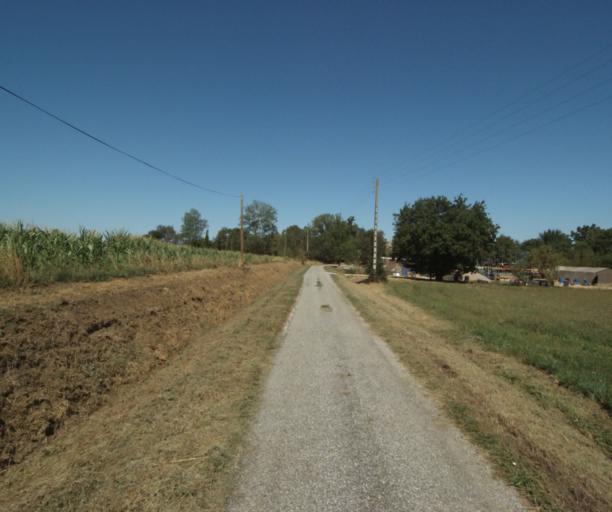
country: FR
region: Midi-Pyrenees
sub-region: Departement de la Haute-Garonne
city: Revel
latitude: 43.4749
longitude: 1.9852
